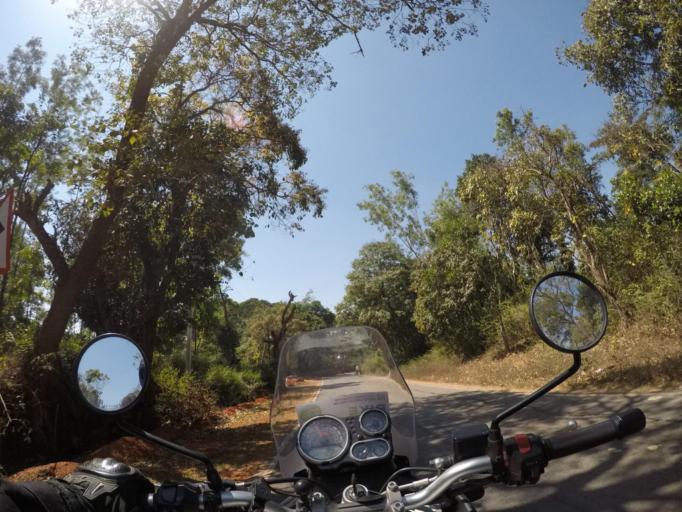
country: IN
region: Karnataka
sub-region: Hassan
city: Sakleshpur
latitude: 12.9384
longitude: 75.7585
